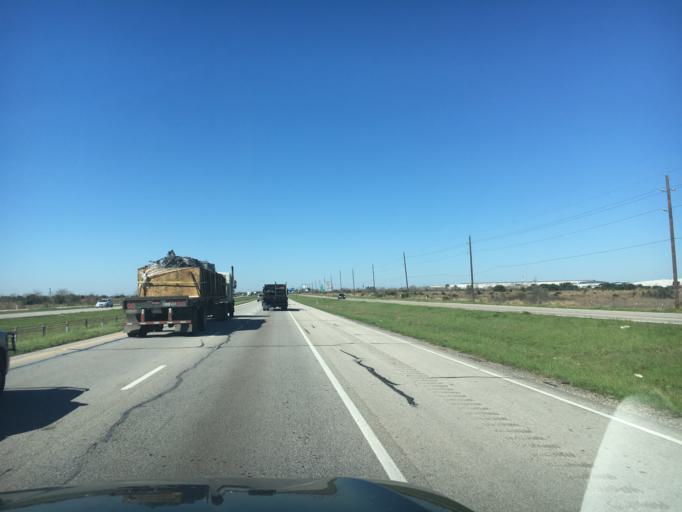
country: US
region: Texas
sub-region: Austin County
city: Sealy
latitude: 29.7613
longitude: -96.2066
